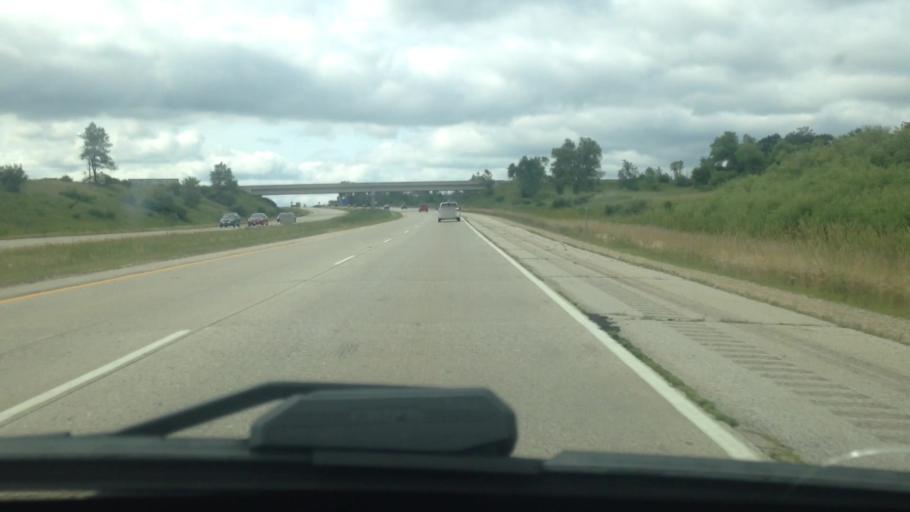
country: US
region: Wisconsin
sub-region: Washington County
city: Jackson
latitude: 43.2978
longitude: -88.1871
